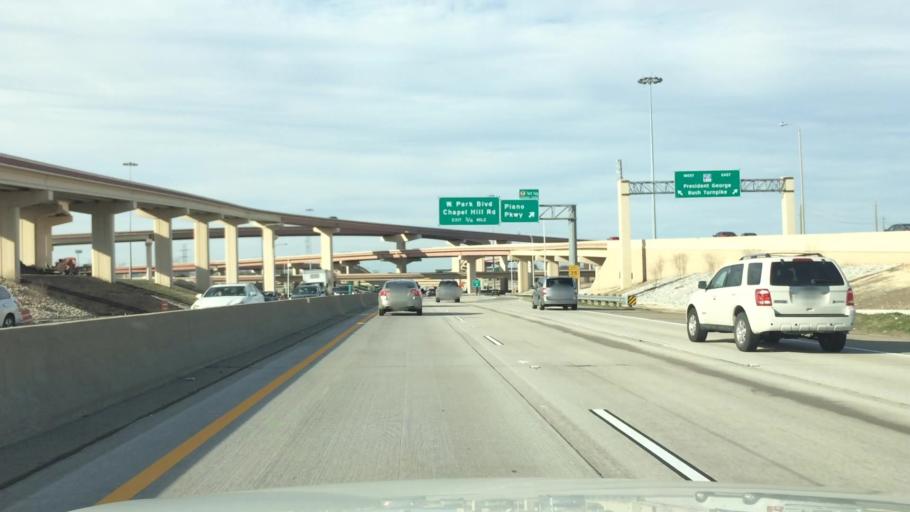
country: US
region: Texas
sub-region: Dallas County
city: Addison
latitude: 33.0100
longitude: -96.8291
